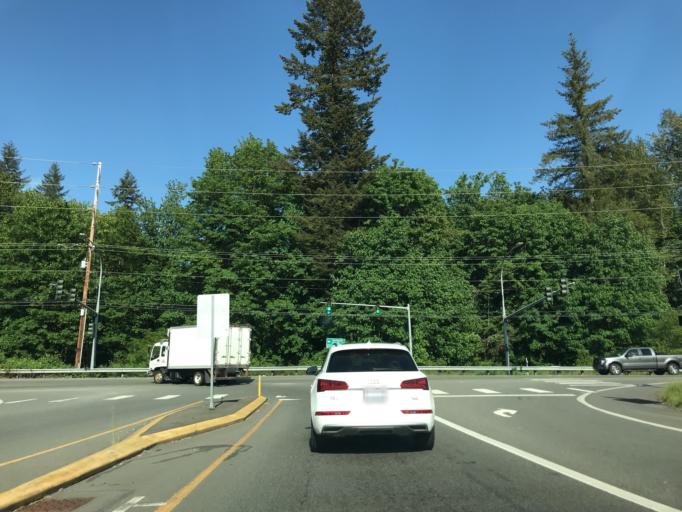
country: US
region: Washington
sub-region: King County
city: Hobart
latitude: 47.4338
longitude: -121.9733
